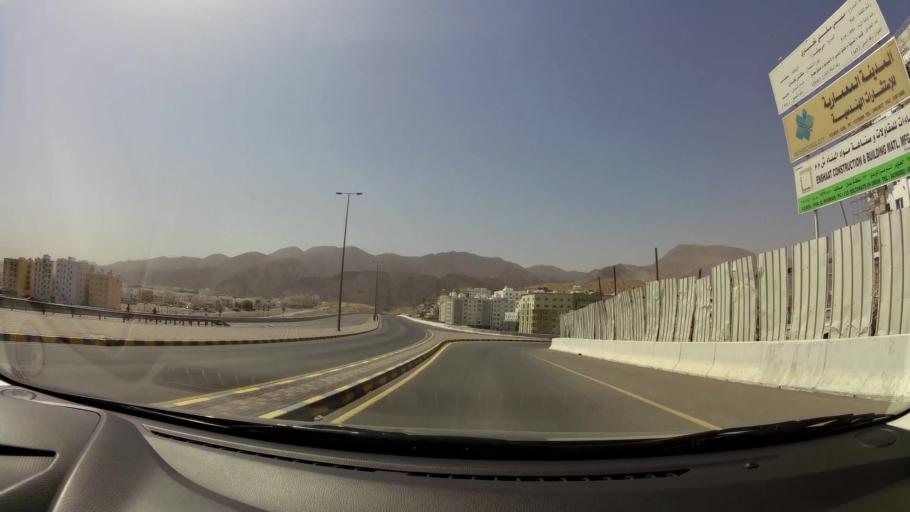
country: OM
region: Muhafazat Masqat
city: Bawshar
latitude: 23.5793
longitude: 58.4173
